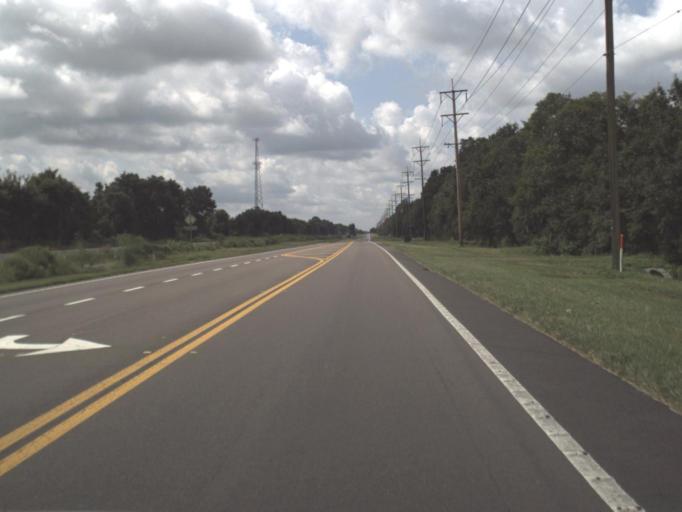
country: US
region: Florida
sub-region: Pasco County
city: Crystal Springs
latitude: 28.1088
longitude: -82.1441
